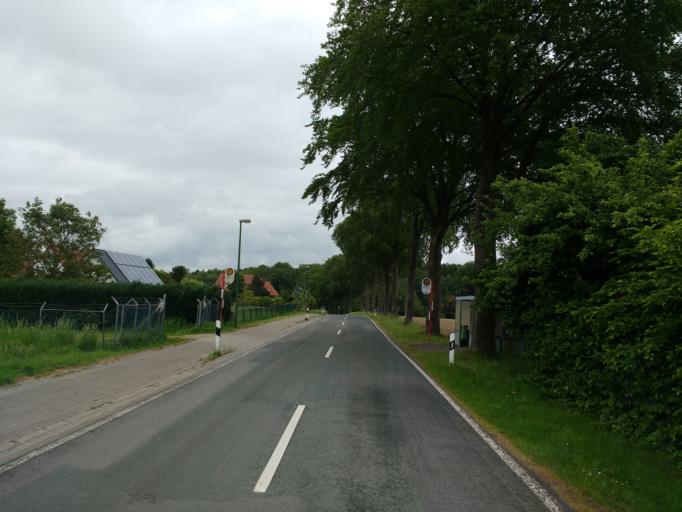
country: DE
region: Lower Saxony
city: Hilter
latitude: 52.1774
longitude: 8.1034
